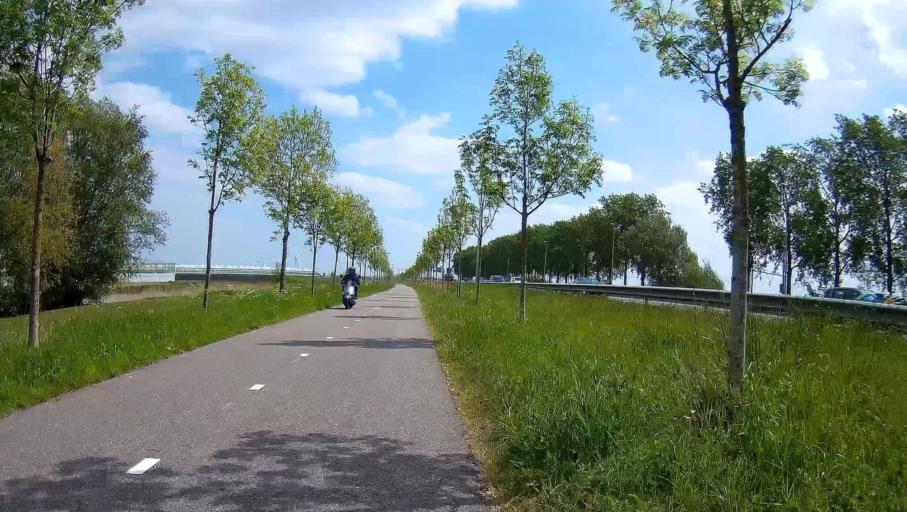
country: NL
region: South Holland
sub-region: Gemeente Waddinxveen
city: Groenswaard
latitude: 52.0237
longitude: 4.5926
